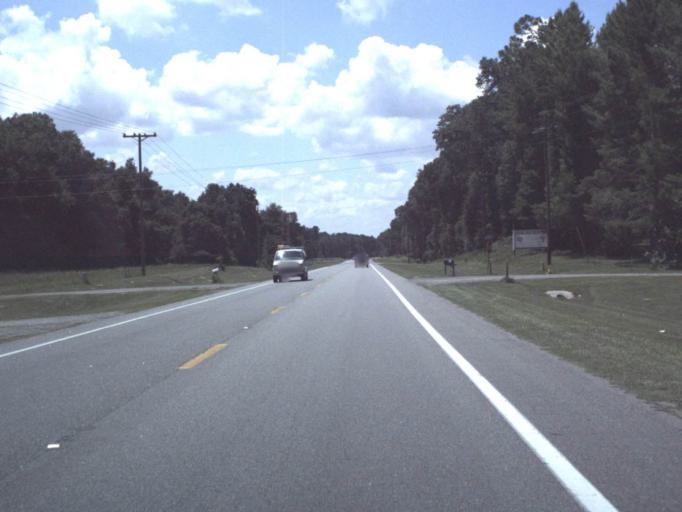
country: US
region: Florida
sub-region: Alachua County
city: High Springs
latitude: 29.9106
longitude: -82.7000
